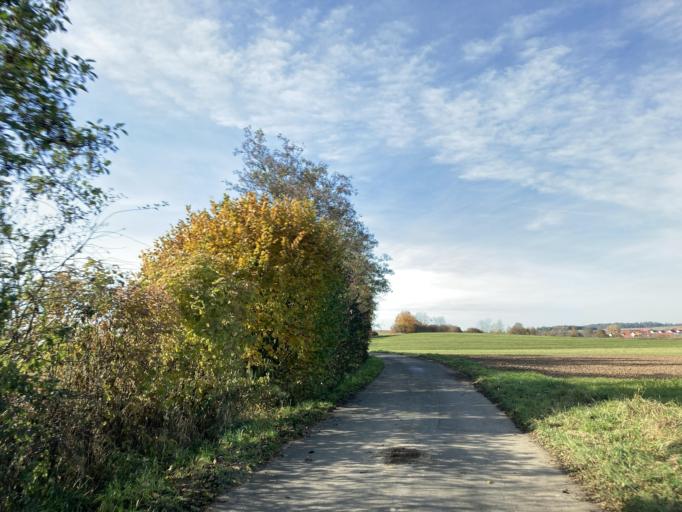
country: DE
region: Baden-Wuerttemberg
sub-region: Tuebingen Region
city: Hirrlingen
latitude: 48.4100
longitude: 8.9264
